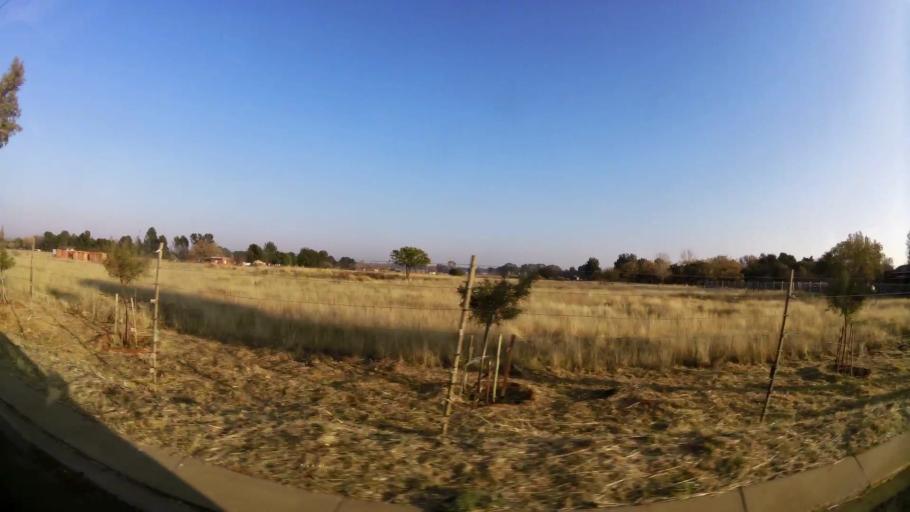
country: ZA
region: Orange Free State
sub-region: Mangaung Metropolitan Municipality
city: Bloemfontein
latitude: -29.0854
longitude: 26.1444
